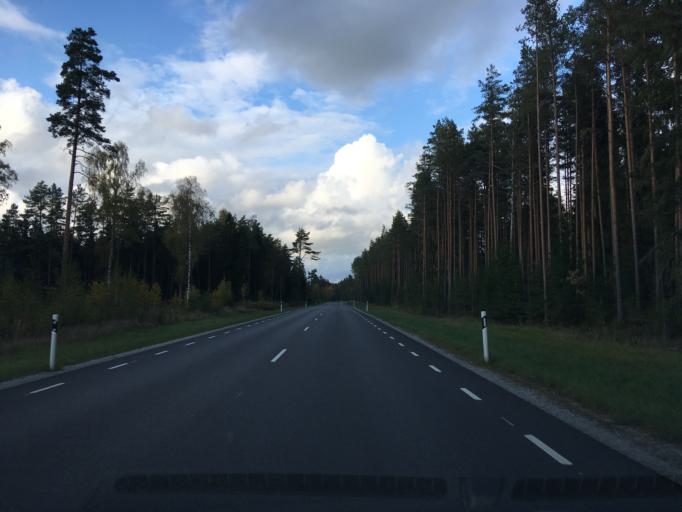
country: EE
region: Harju
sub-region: Nissi vald
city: Turba
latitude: 59.1416
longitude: 24.0761
